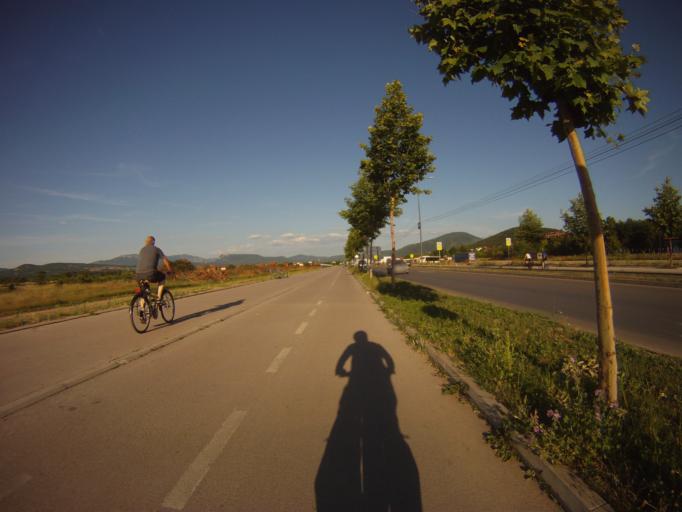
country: RS
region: Central Serbia
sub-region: Nisavski Okrug
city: Nis
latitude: 43.3080
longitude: 21.9490
